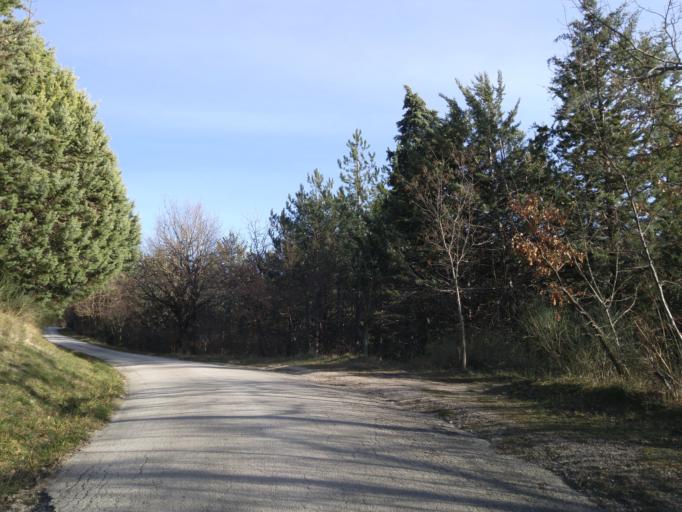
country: IT
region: The Marches
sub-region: Provincia di Pesaro e Urbino
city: Canavaccio
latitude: 43.6771
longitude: 12.6791
